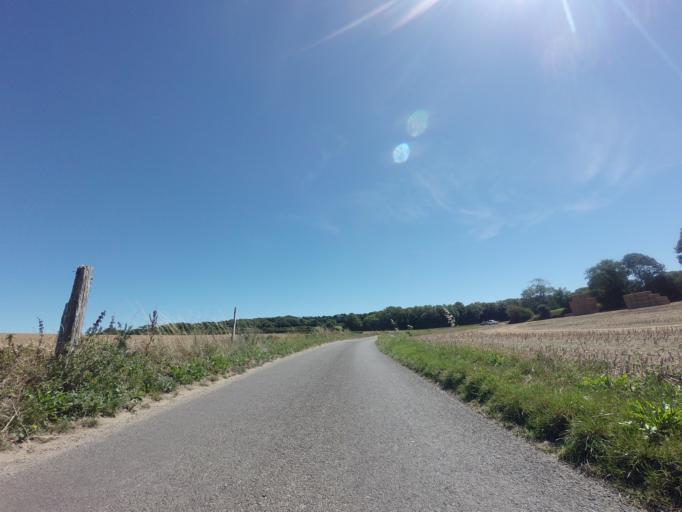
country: GB
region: England
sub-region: Kent
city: Deal
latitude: 51.1920
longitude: 1.3661
